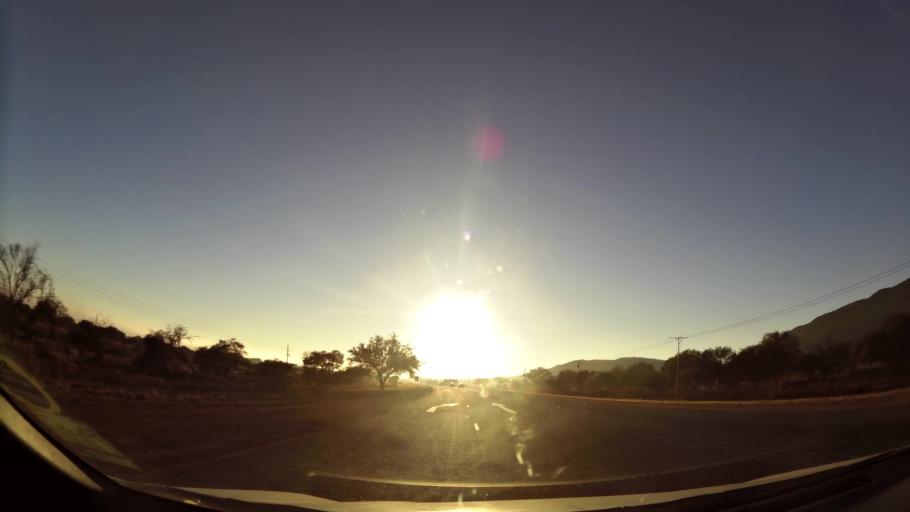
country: ZA
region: Limpopo
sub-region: Capricorn District Municipality
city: Polokwane
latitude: -24.0130
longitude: 29.3222
